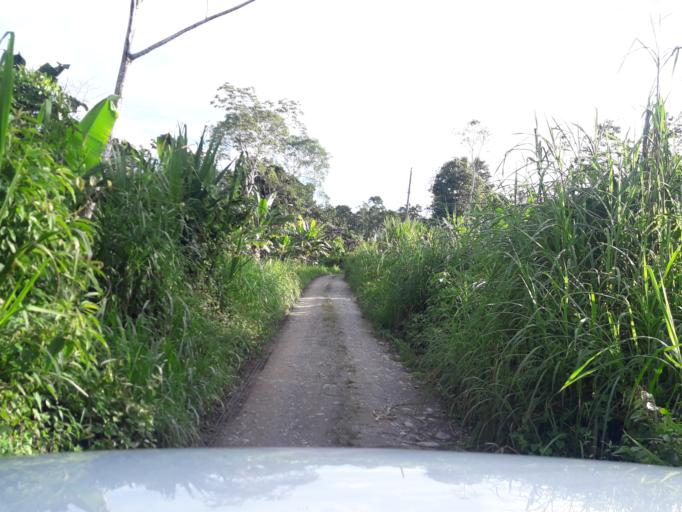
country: EC
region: Orellana
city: Boca Suno
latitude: -0.8891
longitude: -77.3035
